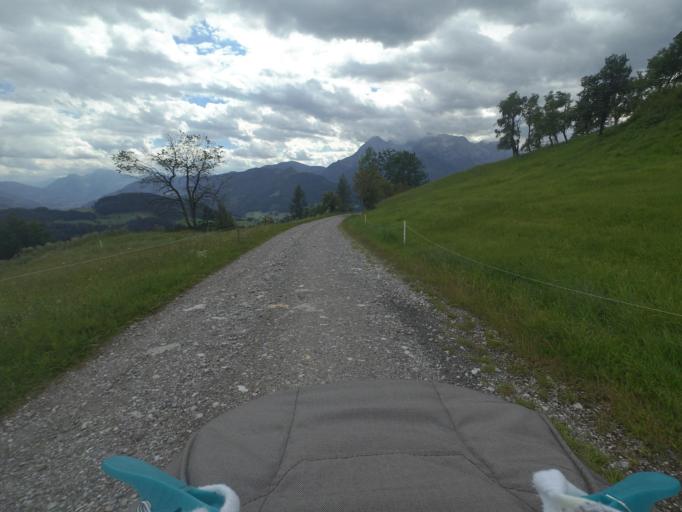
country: AT
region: Salzburg
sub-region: Politischer Bezirk Sankt Johann im Pongau
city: Werfenweng
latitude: 47.4682
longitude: 13.2387
